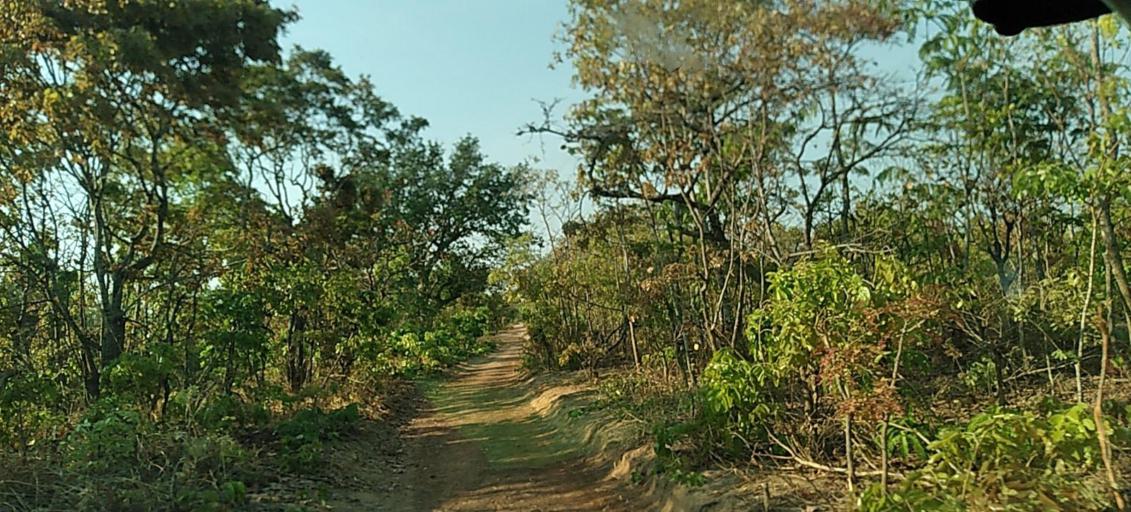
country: ZM
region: North-Western
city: Kalengwa
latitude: -13.1559
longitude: 25.0340
